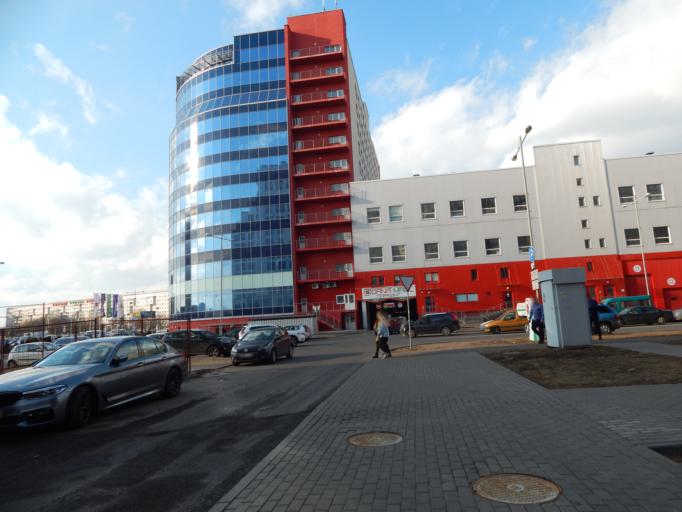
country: BY
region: Minsk
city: Borovlyany
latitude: 53.9322
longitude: 27.6505
